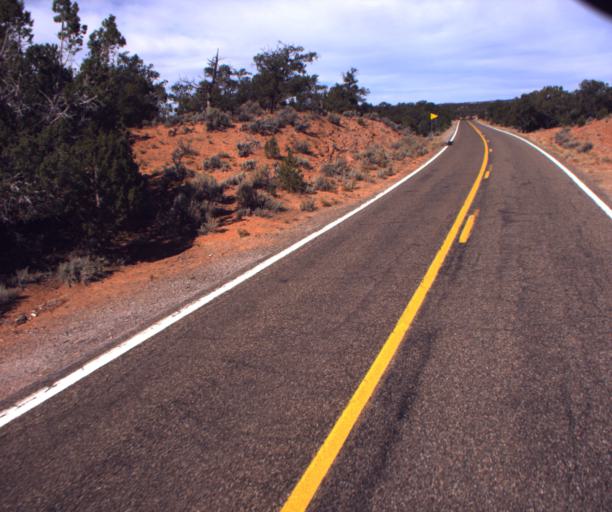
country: US
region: Arizona
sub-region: Navajo County
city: Kayenta
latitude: 36.6031
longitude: -110.4982
